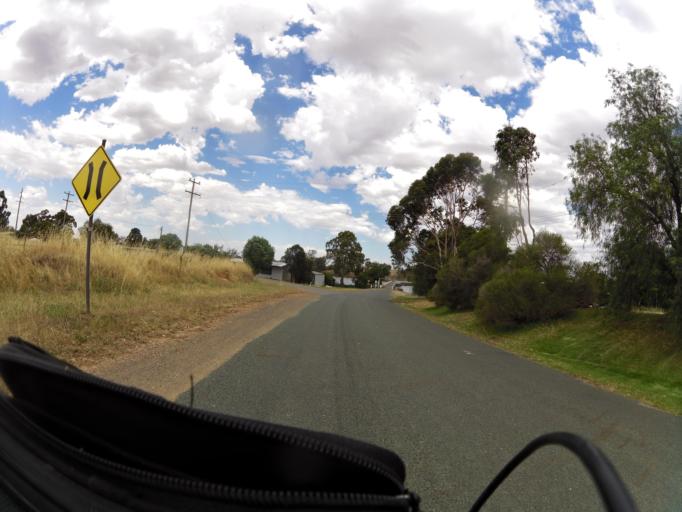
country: AU
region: Victoria
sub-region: Campaspe
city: Kyabram
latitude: -36.7437
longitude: 145.1378
